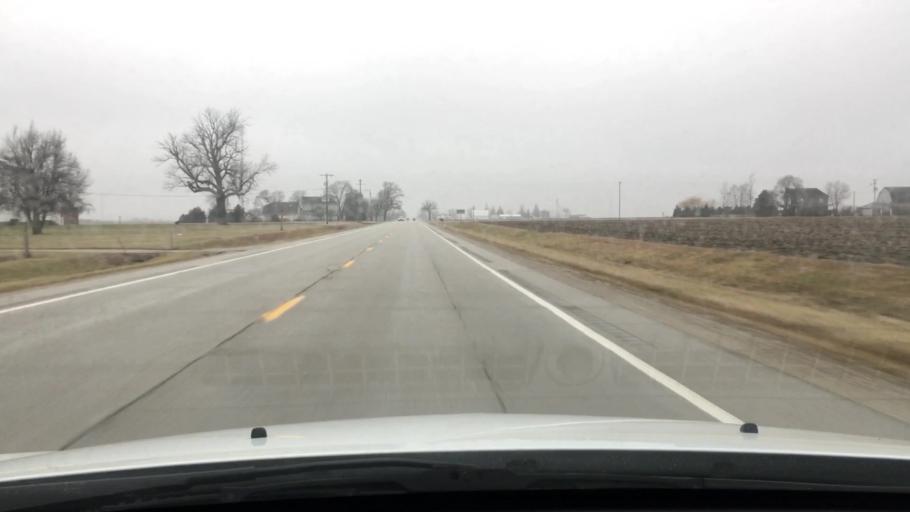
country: US
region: Illinois
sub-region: Livingston County
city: Flanagan
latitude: 40.8709
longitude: -88.8701
